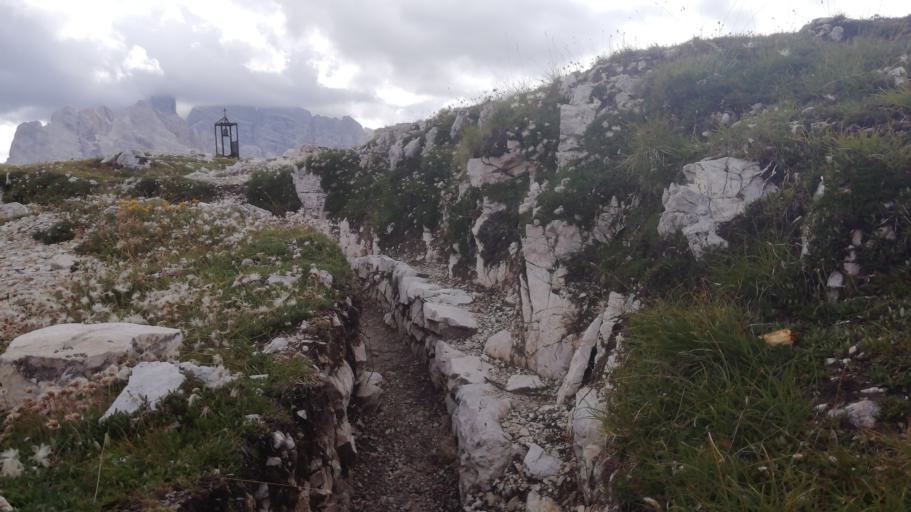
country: IT
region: Trentino-Alto Adige
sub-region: Bolzano
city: Dobbiaco
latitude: 46.6205
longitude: 12.2476
